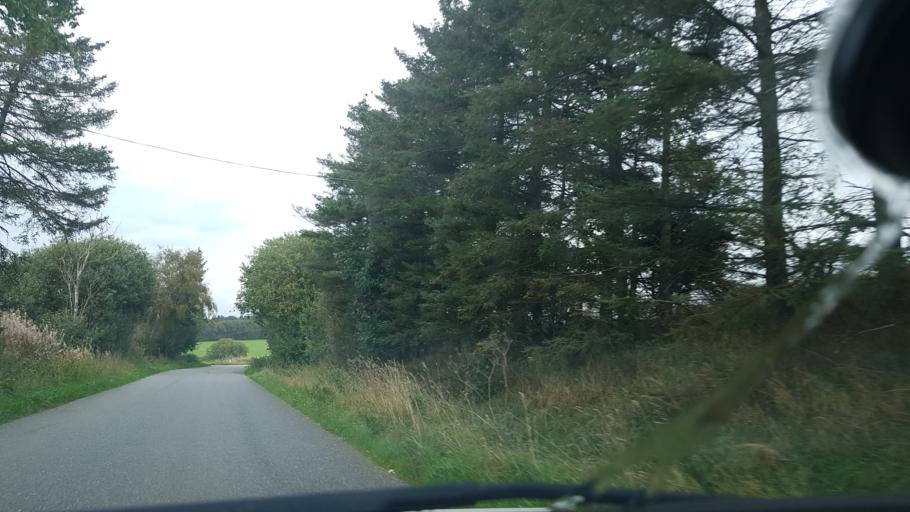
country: DK
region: South Denmark
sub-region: Vejle Kommune
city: Egtved
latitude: 55.5879
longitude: 9.1966
